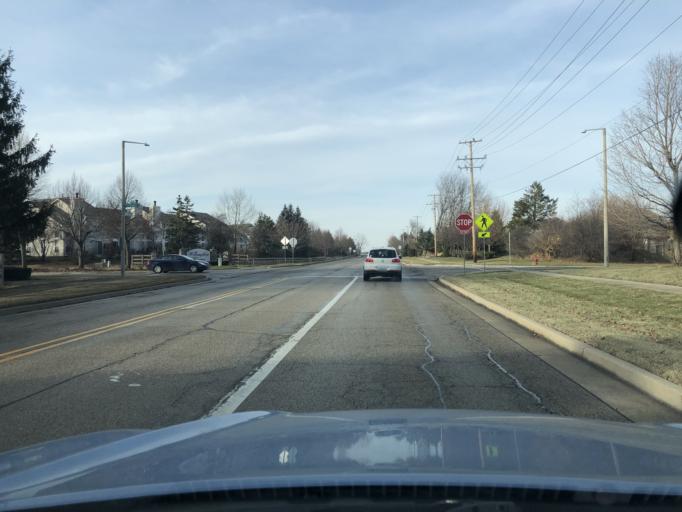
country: US
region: Illinois
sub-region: McHenry County
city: Lake in the Hills
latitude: 42.1540
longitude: -88.3265
